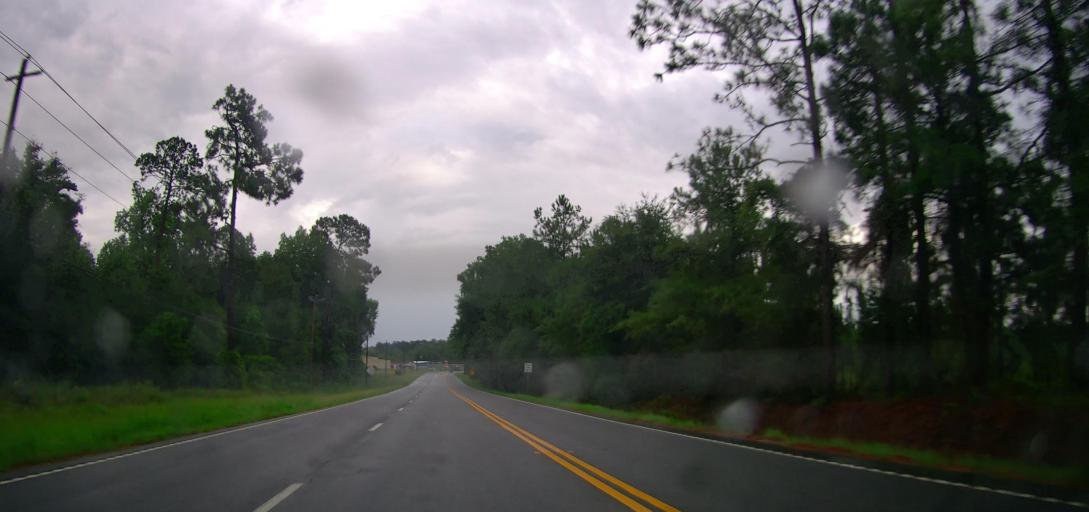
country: US
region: Georgia
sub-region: Ware County
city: Deenwood
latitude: 31.2605
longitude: -82.3833
